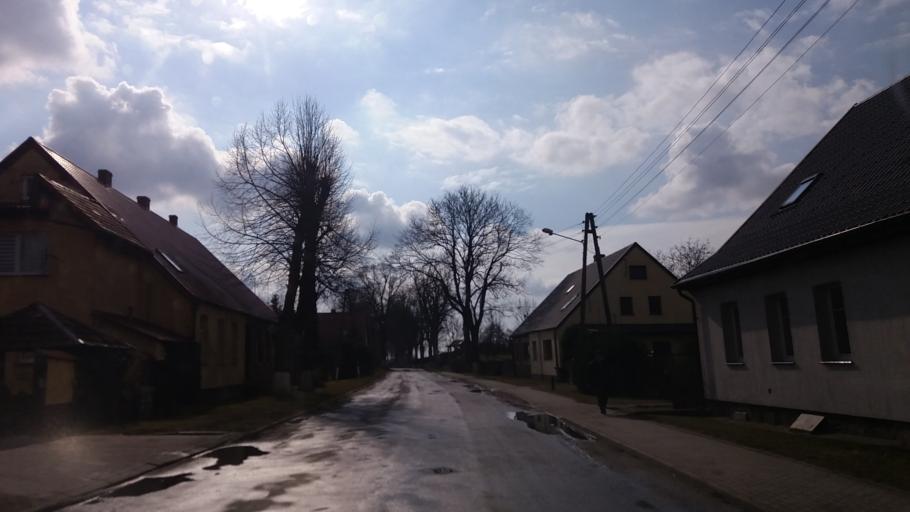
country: PL
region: West Pomeranian Voivodeship
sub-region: Powiat choszczenski
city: Recz
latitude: 53.1850
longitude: 15.5876
